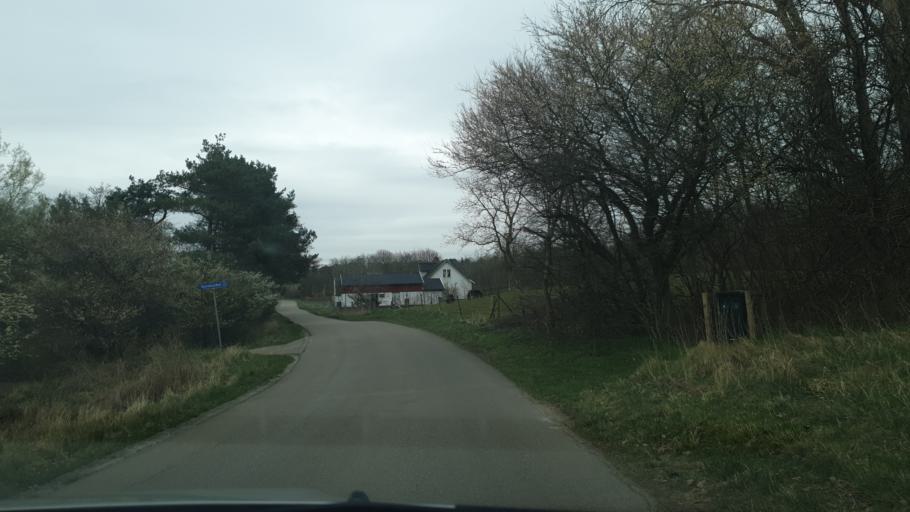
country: DK
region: Zealand
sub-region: Odsherred Kommune
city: Asnaes
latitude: 55.8356
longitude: 11.4288
